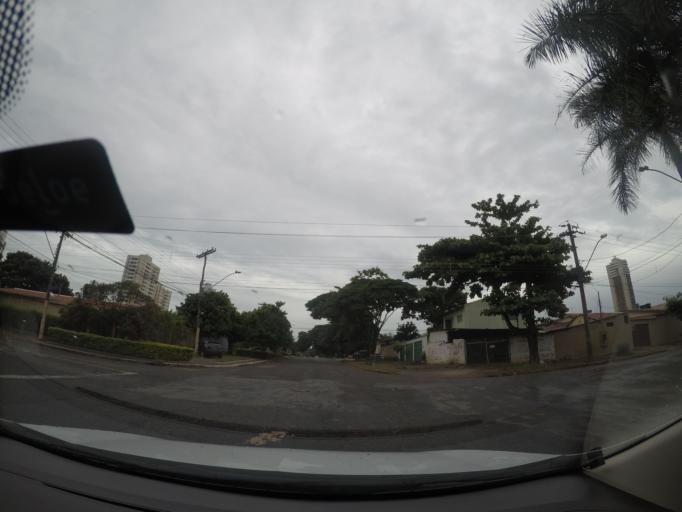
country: BR
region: Goias
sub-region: Goiania
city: Goiania
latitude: -16.6803
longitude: -49.2396
